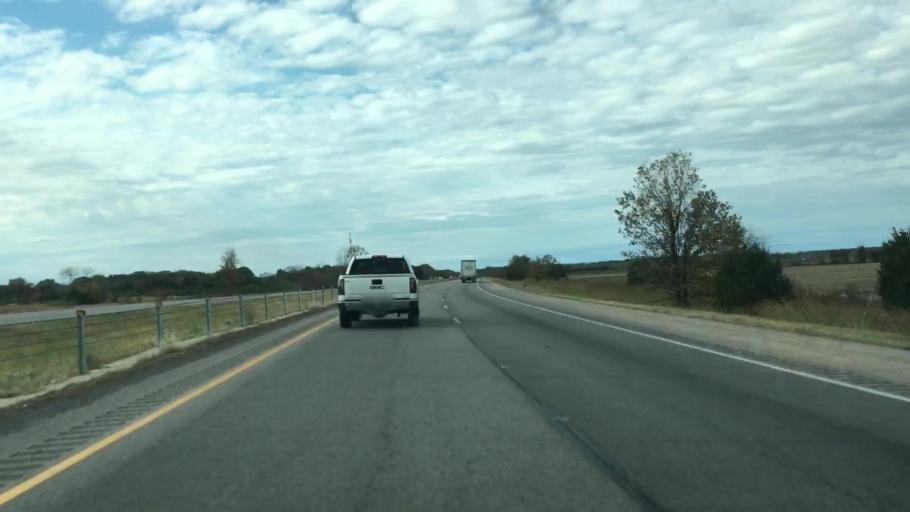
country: US
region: Arkansas
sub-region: Conway County
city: Morrilton
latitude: 35.1969
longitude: -92.8013
